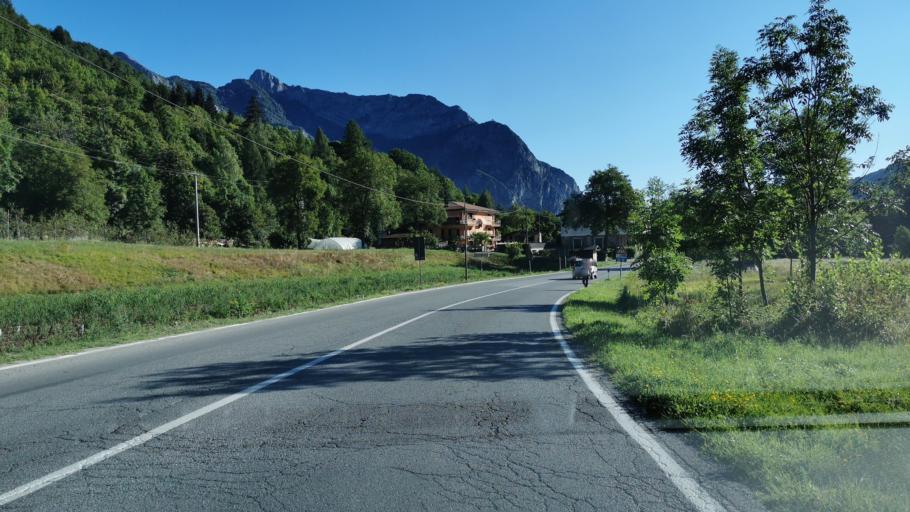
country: IT
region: Piedmont
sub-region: Provincia di Cuneo
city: Valdieri
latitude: 44.2647
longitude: 7.3812
